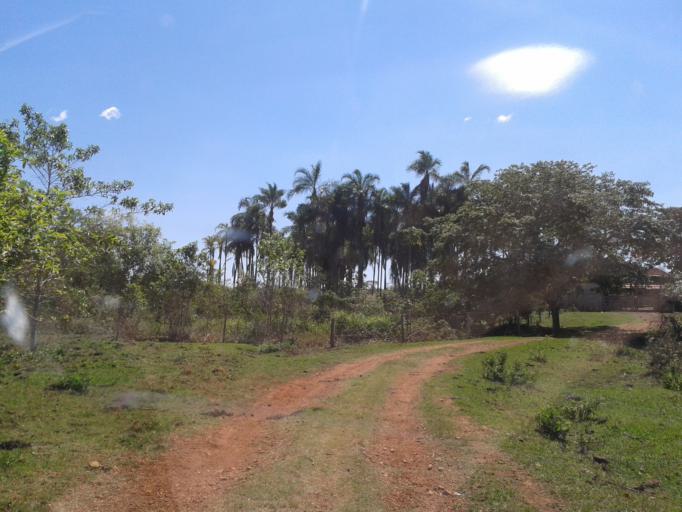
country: BR
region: Minas Gerais
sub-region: Monte Alegre De Minas
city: Monte Alegre de Minas
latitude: -18.7973
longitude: -49.0740
